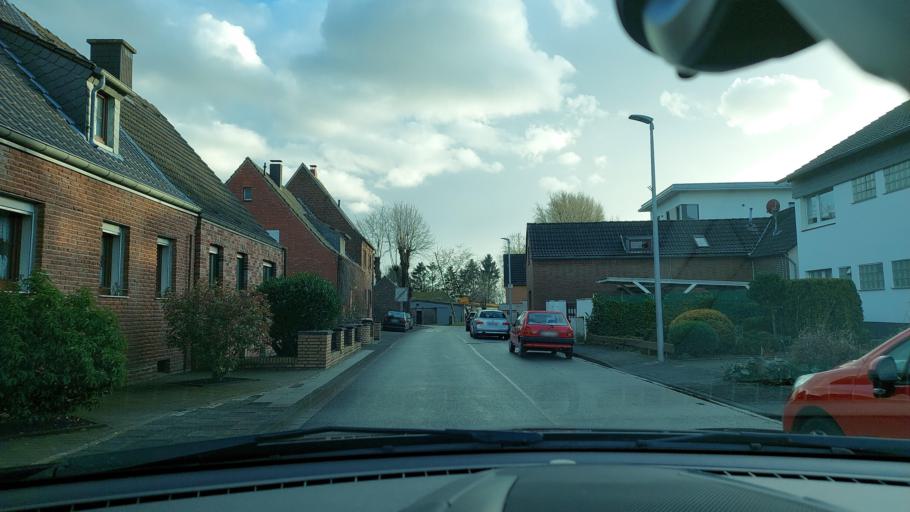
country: DE
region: North Rhine-Westphalia
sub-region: Regierungsbezirk Koln
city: Sinnersdorf
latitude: 51.0545
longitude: 6.8176
